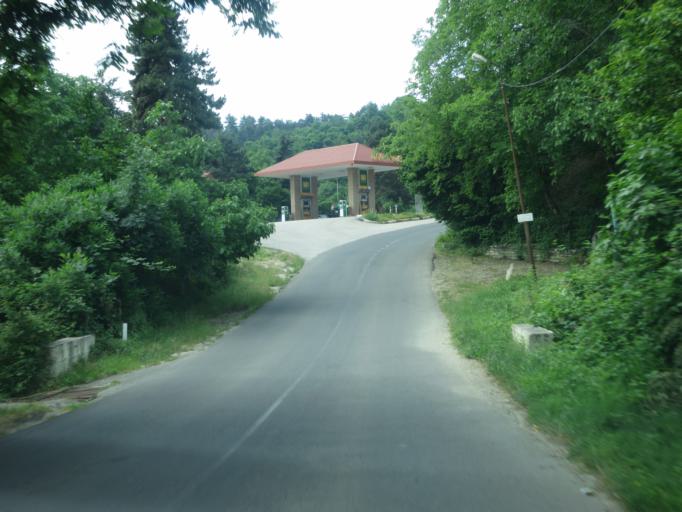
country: GE
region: Kakheti
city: Sighnaghi
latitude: 41.6125
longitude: 45.9239
